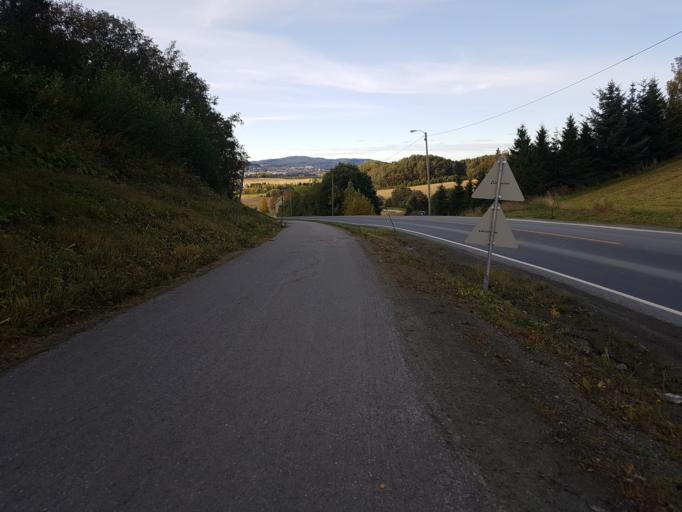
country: NO
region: Sor-Trondelag
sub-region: Trondheim
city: Trondheim
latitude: 63.3686
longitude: 10.4413
